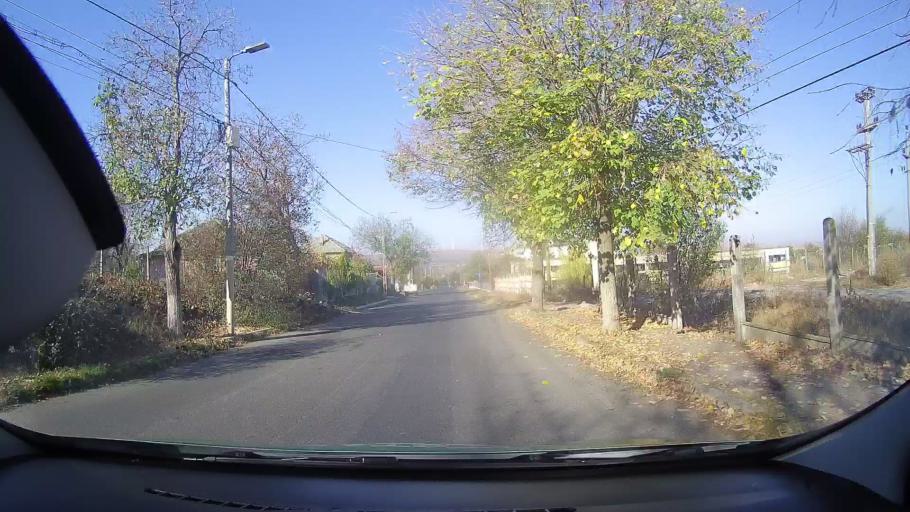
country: RO
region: Tulcea
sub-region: Oras Babadag
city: Babadag
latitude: 44.8867
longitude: 28.7342
